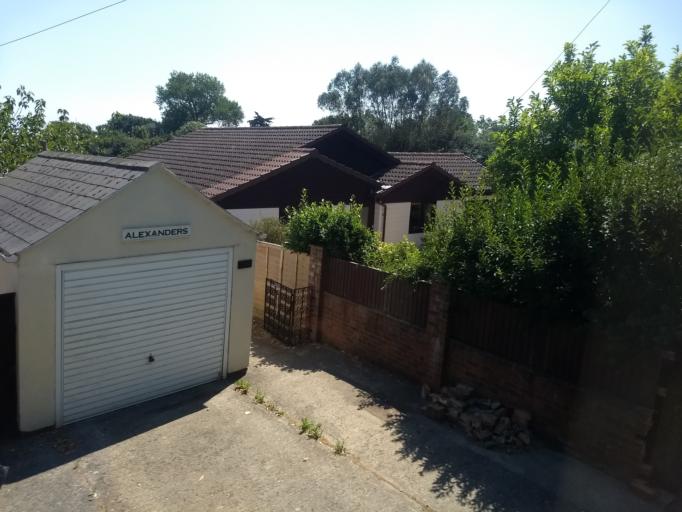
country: GB
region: England
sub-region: Isle of Wight
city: Ryde
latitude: 50.7182
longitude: -1.1465
